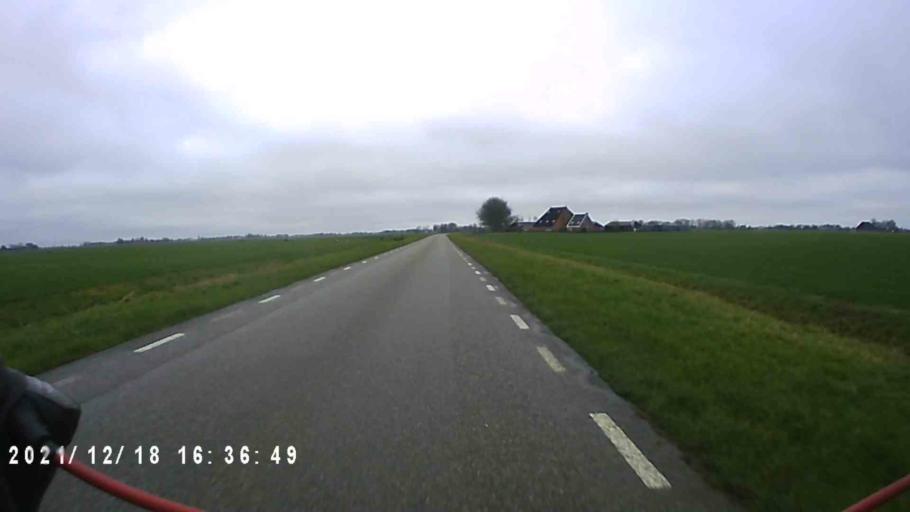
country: NL
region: Friesland
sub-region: Gemeente Dongeradeel
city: Dokkum
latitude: 53.3575
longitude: 6.0190
